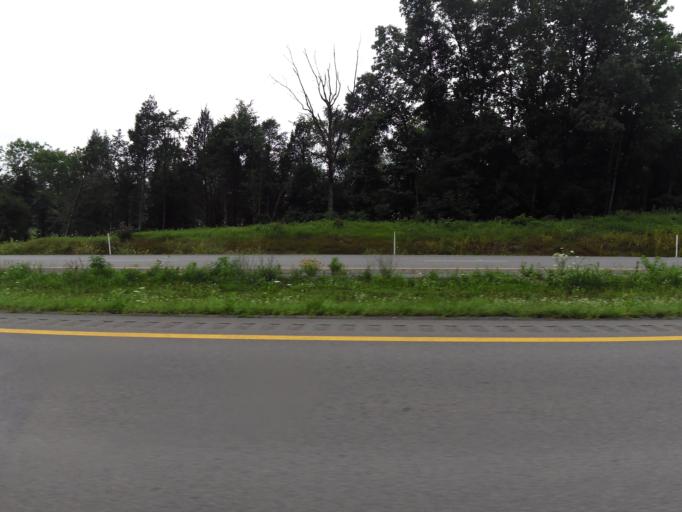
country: US
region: Kentucky
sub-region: Grayson County
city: Leitchfield
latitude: 37.4129
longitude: -86.4229
